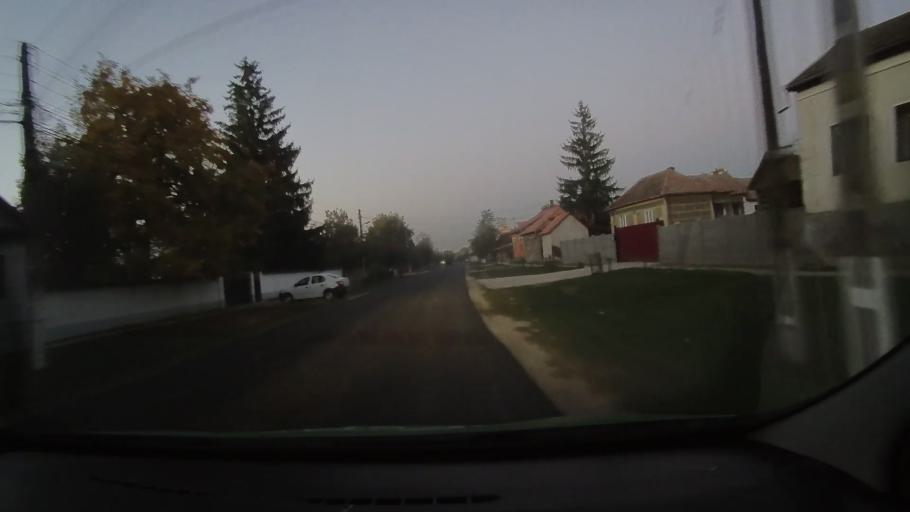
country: RO
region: Bihor
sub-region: Comuna Simian
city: Simian
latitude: 47.4957
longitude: 22.0896
